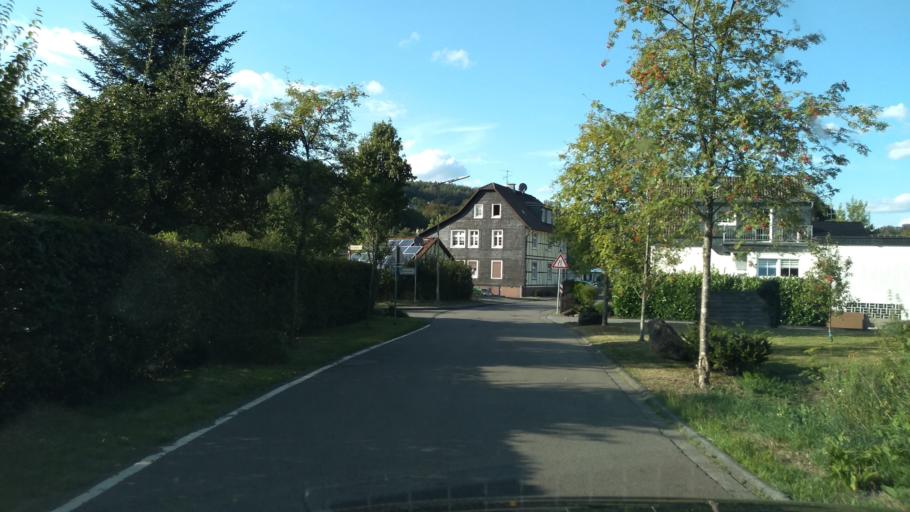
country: DE
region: North Rhine-Westphalia
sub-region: Regierungsbezirk Koln
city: Engelskirchen
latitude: 50.9854
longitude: 7.4561
